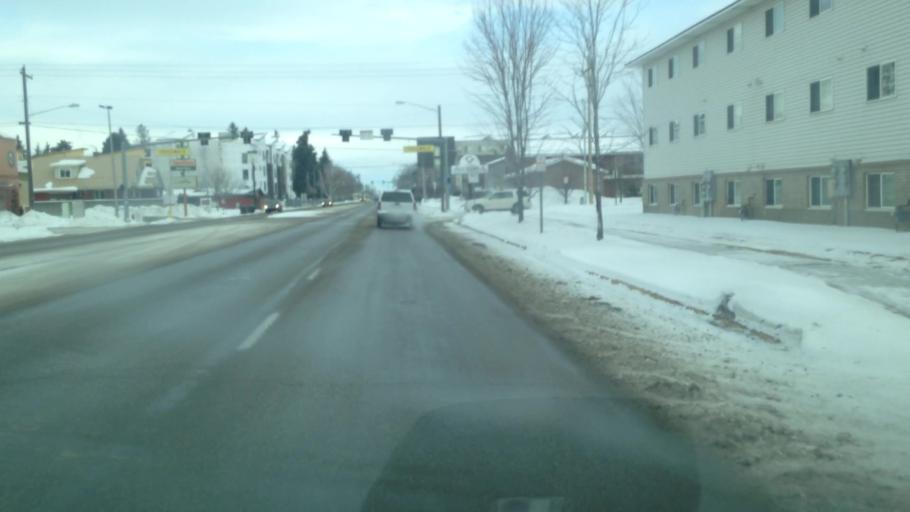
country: US
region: Idaho
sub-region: Madison County
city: Rexburg
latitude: 43.8192
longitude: -111.7895
